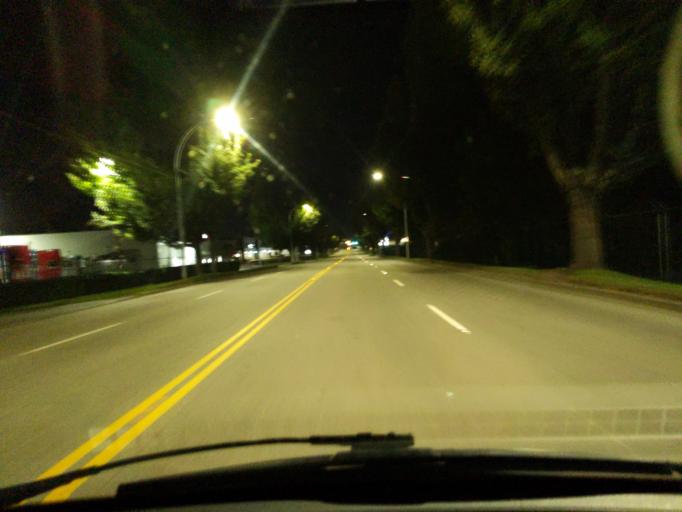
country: CA
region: British Columbia
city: Walnut Grove
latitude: 49.1769
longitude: -122.6830
